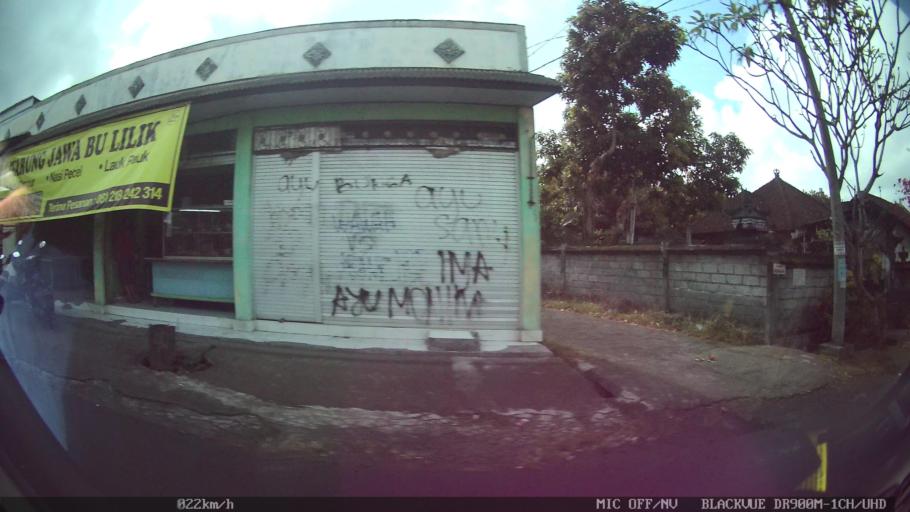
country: ID
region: Bali
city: Banjar Batur
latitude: -8.6043
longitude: 115.2061
